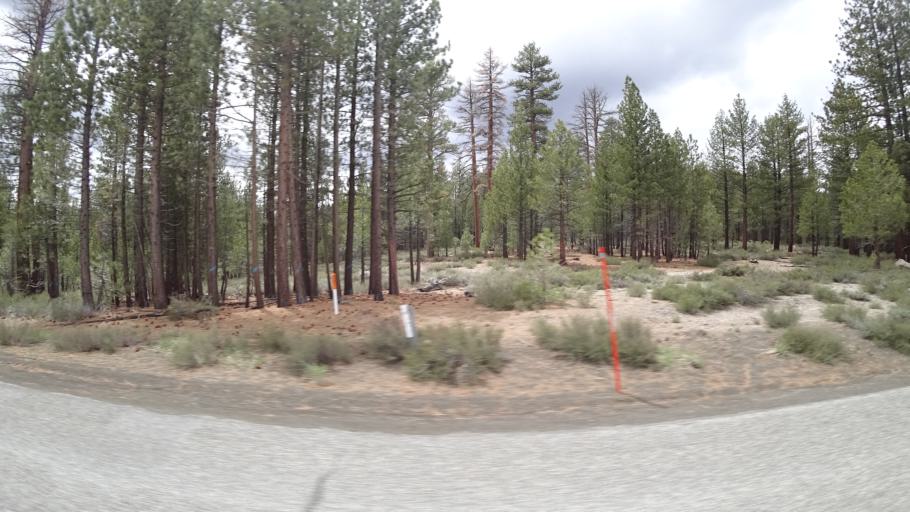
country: US
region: California
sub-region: Mono County
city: Mammoth Lakes
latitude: 37.7137
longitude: -118.9550
